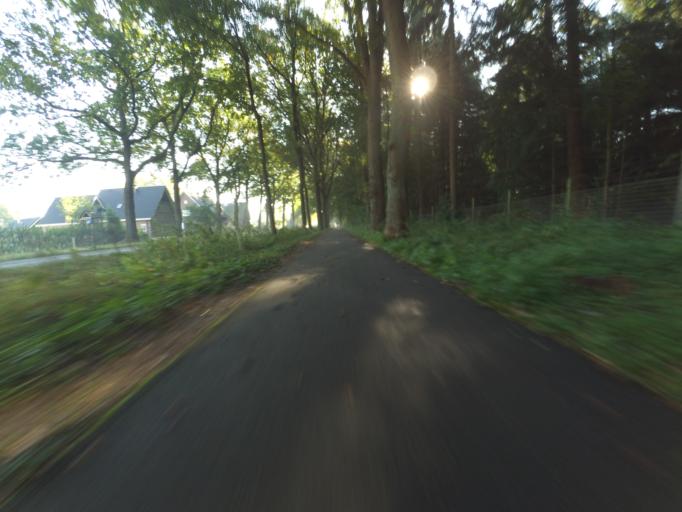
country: NL
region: Gelderland
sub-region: Gemeente Apeldoorn
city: Apeldoorn
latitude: 52.2421
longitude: 5.9536
